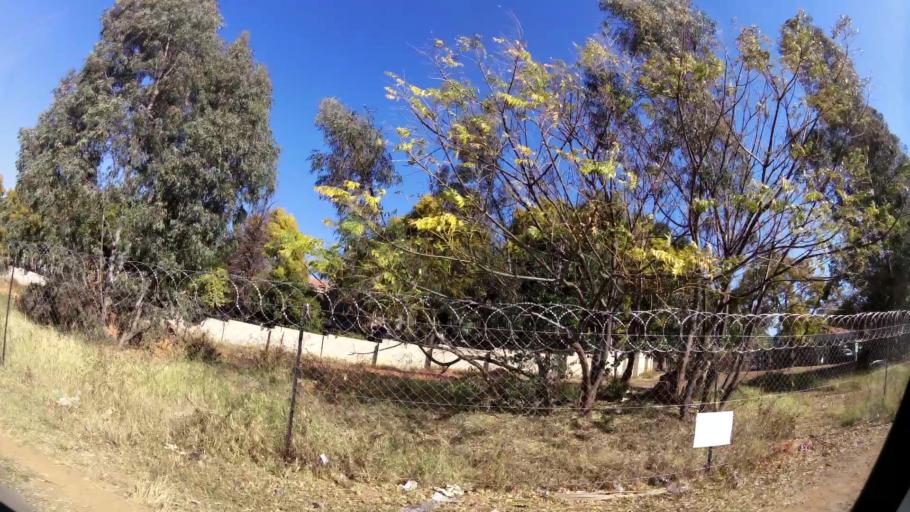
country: ZA
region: Gauteng
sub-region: City of Tshwane Metropolitan Municipality
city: Pretoria
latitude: -25.7847
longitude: 28.2672
